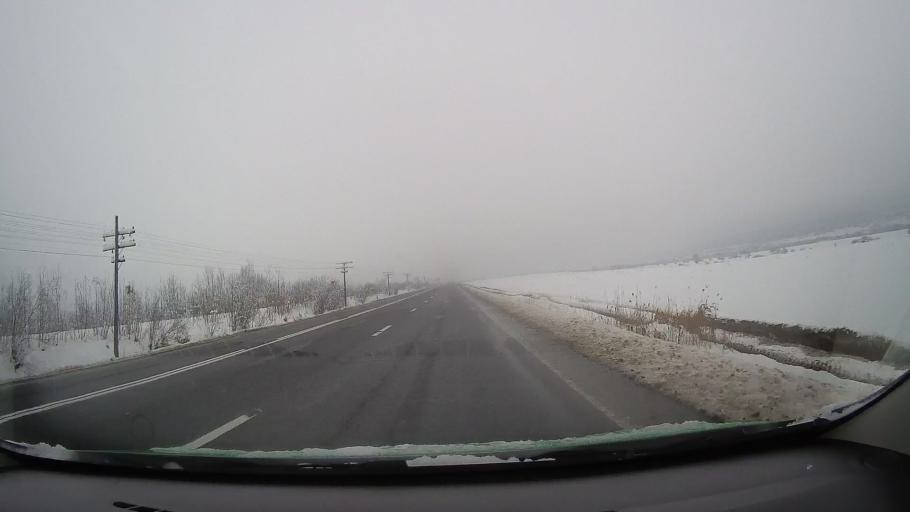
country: RO
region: Sibiu
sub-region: Oras Saliste
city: Saliste
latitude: 45.7957
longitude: 23.9111
